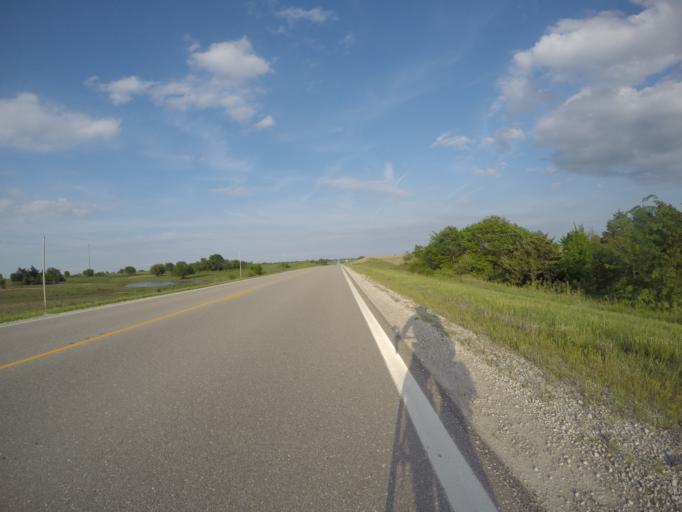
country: US
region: Kansas
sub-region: Pottawatomie County
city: Westmoreland
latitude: 39.4282
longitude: -96.6040
